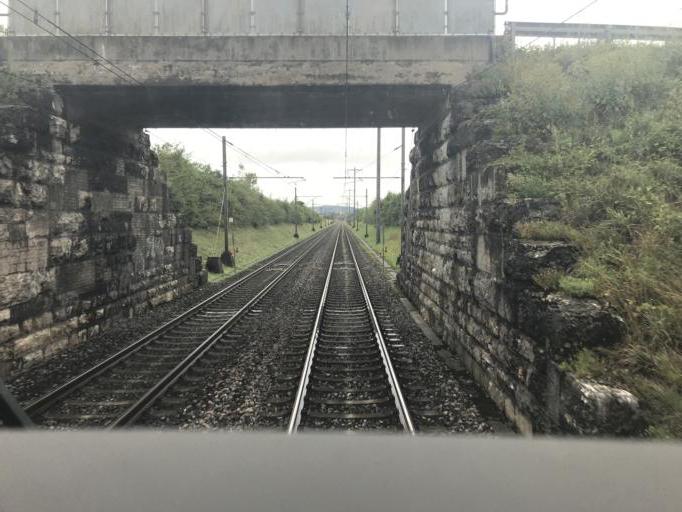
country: CH
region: Zurich
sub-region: Bezirk Dielsdorf
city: Niederglatt / Niederglatt (Dorfkern)
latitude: 47.4964
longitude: 8.5090
